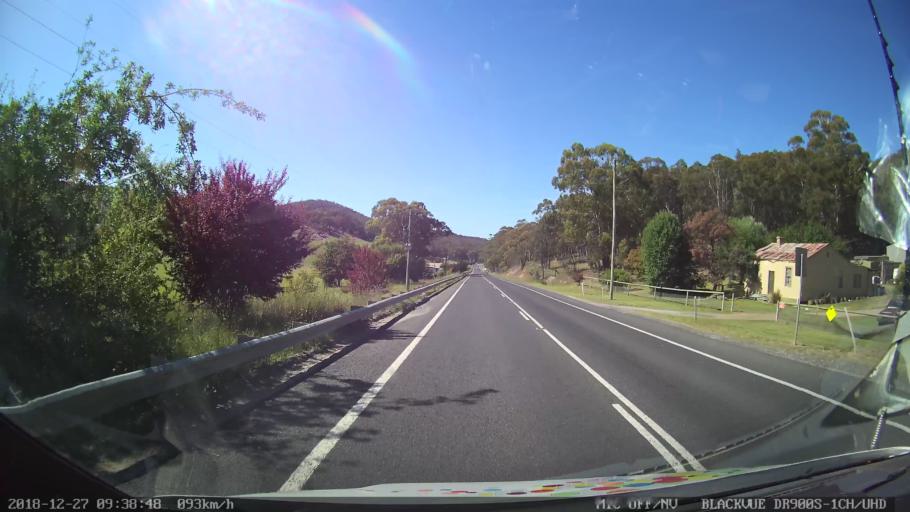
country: AU
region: New South Wales
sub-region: Lithgow
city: Portland
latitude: -33.2849
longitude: 150.0351
